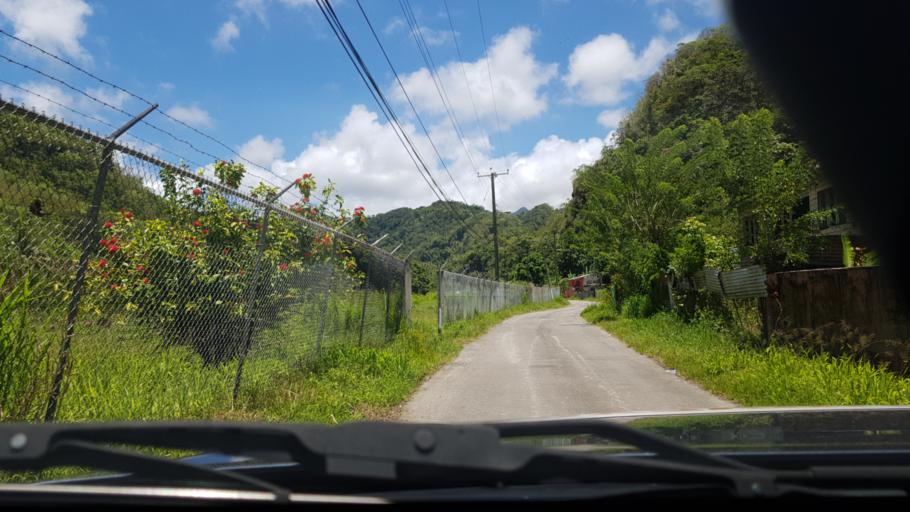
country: LC
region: Anse-la-Raye
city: Canaries
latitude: 13.9023
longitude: -61.0637
